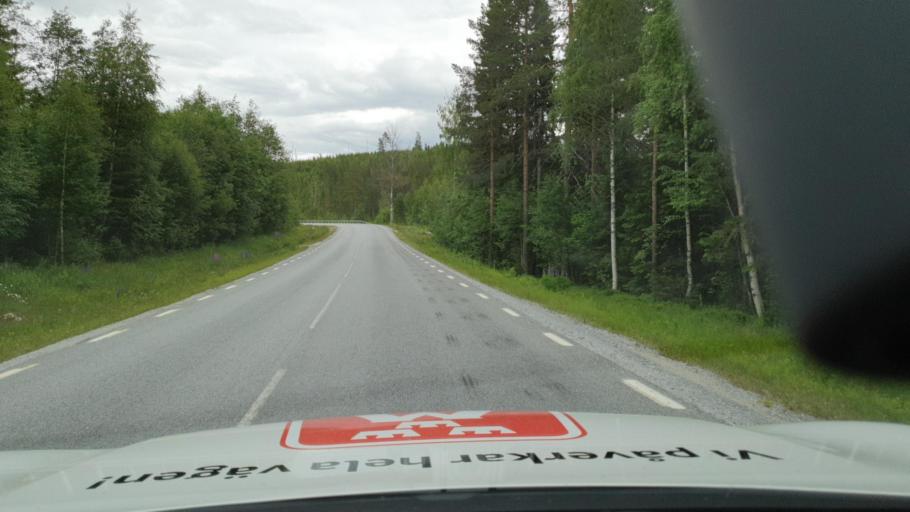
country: SE
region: Vaesterbotten
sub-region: Bjurholms Kommun
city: Bjurholm
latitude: 63.8777
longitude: 19.0100
